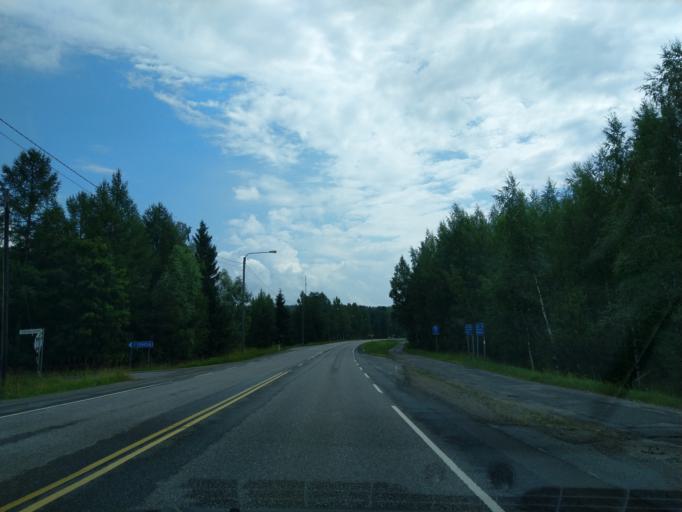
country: FI
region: South Karelia
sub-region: Imatra
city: Parikkala
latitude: 61.5775
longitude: 29.5028
